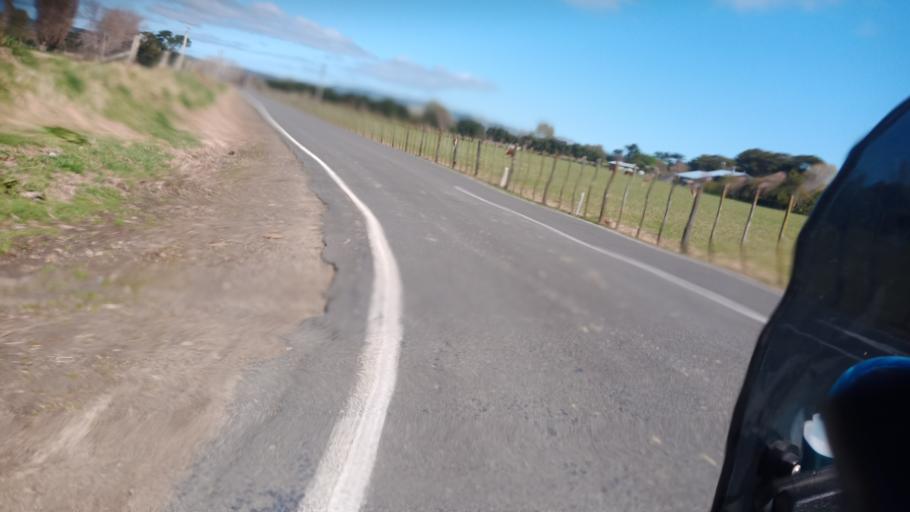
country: NZ
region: Gisborne
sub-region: Gisborne District
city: Gisborne
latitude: -39.0347
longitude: 177.8536
